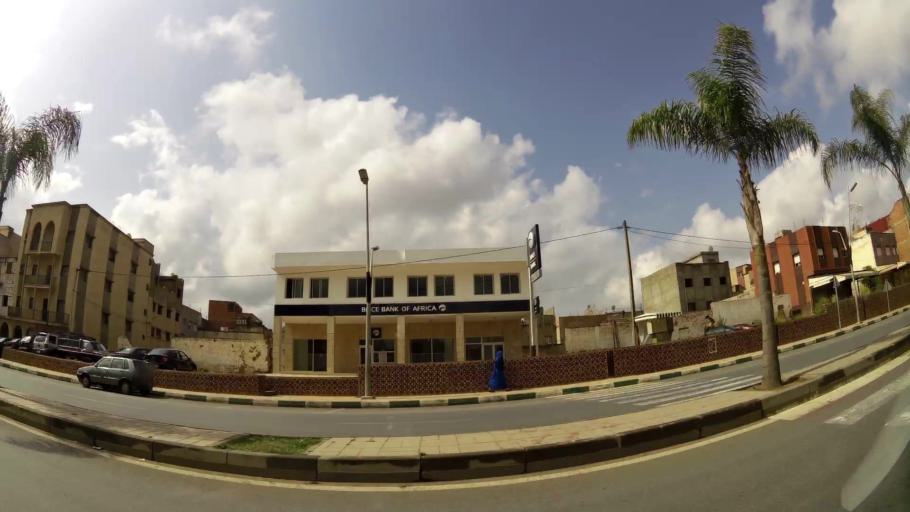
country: MA
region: Rabat-Sale-Zemmour-Zaer
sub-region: Khemisset
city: Tiflet
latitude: 33.8936
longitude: -6.3194
